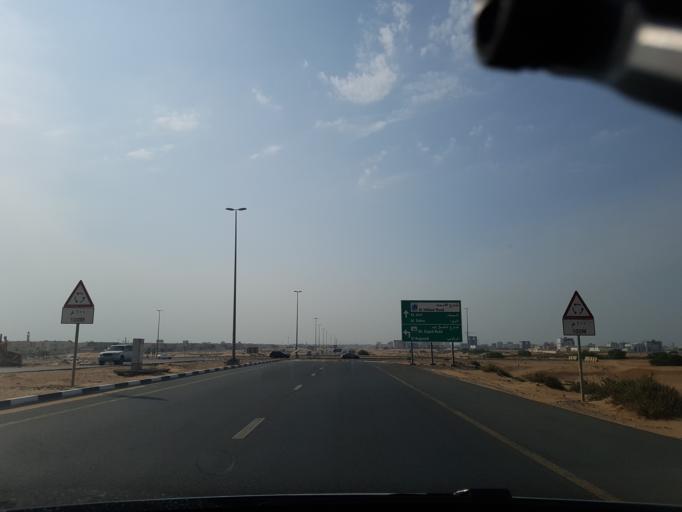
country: AE
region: Ajman
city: Ajman
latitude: 25.4134
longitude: 55.5582
